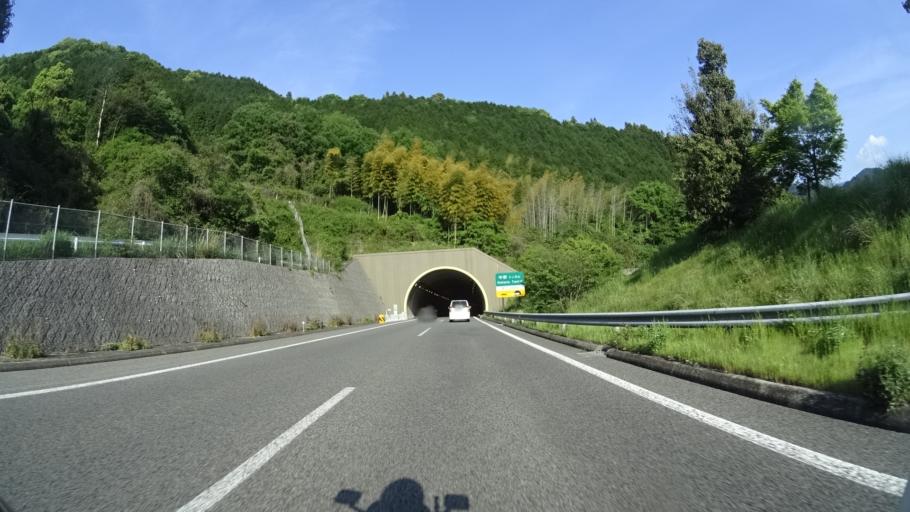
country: JP
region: Ehime
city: Saijo
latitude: 33.8869
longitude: 133.1735
